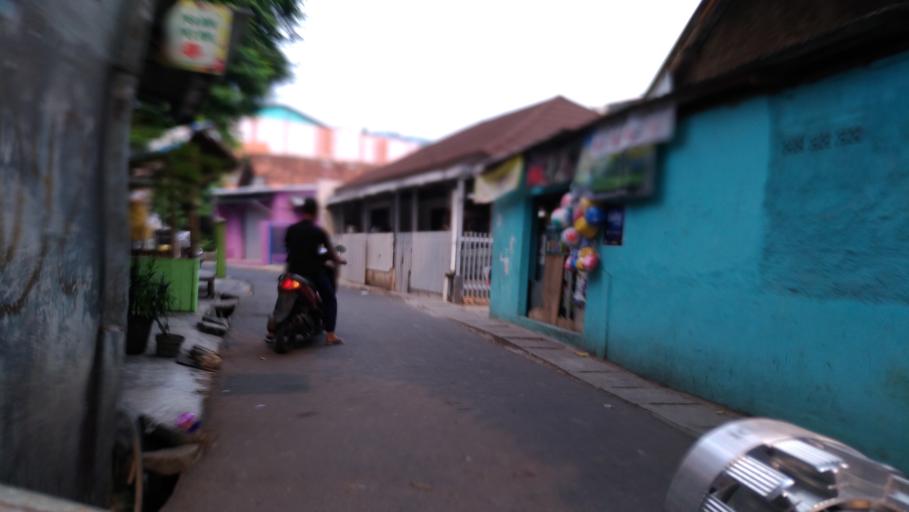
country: ID
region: West Java
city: Depok
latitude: -6.3642
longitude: 106.8573
